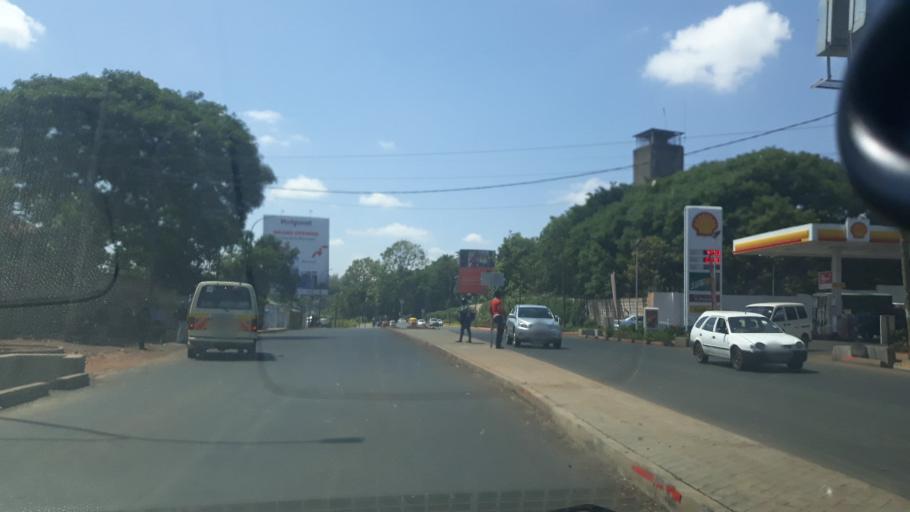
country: KE
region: Nairobi Area
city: Nairobi
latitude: -1.2305
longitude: 36.8038
